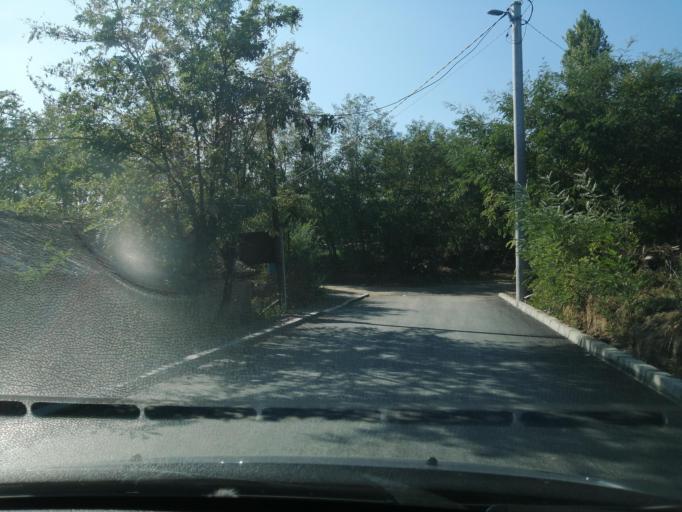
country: MK
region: Bogdanci
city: Bogdanci
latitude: 41.2031
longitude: 22.5693
